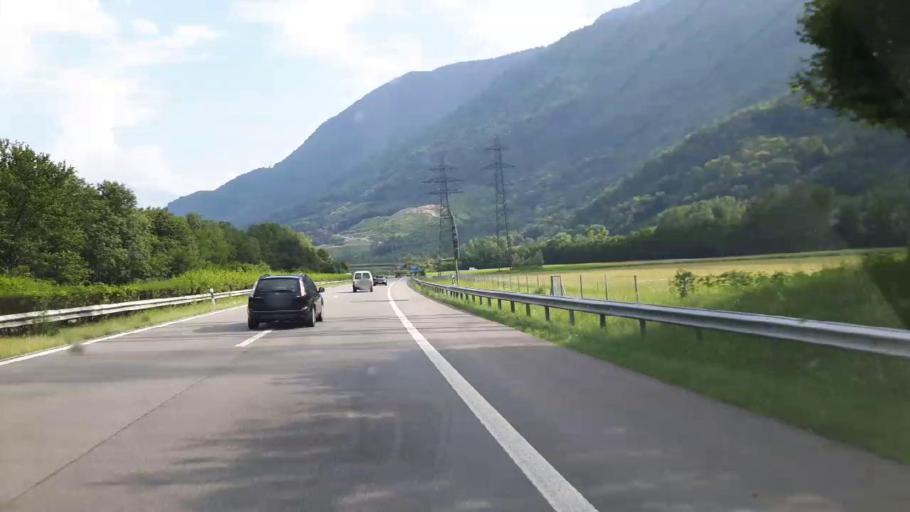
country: CH
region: Ticino
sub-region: Riviera District
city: Claro
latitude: 46.2599
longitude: 9.0096
